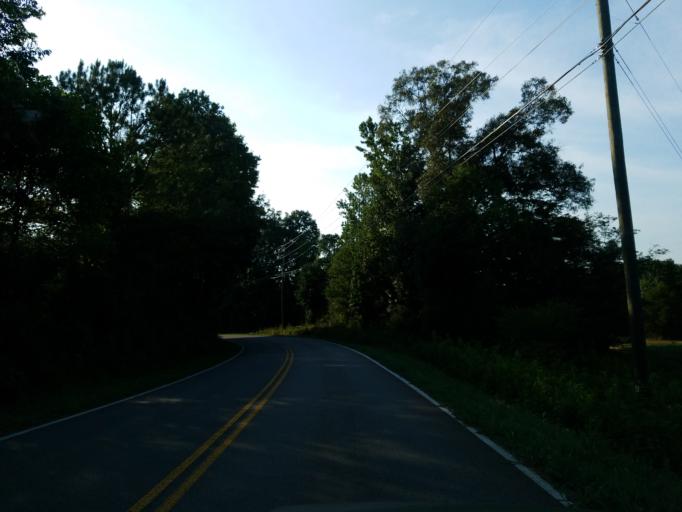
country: US
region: Georgia
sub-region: Pickens County
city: Jasper
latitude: 34.5396
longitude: -84.5357
